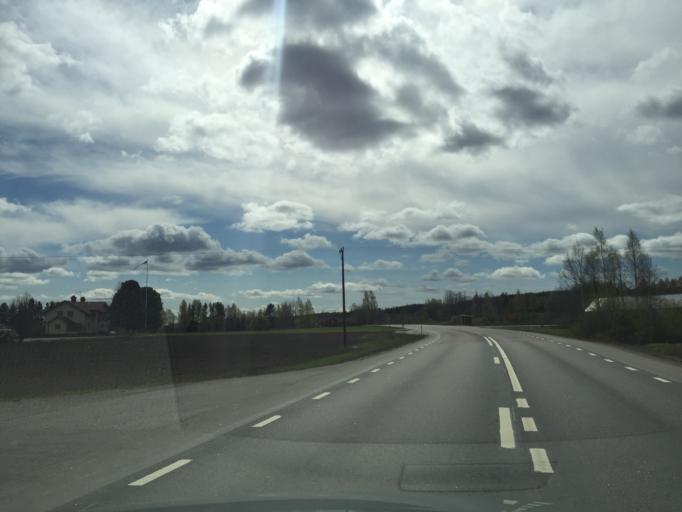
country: SE
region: Gaevleborg
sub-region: Bollnas Kommun
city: Arbra
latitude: 61.5042
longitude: 16.3572
